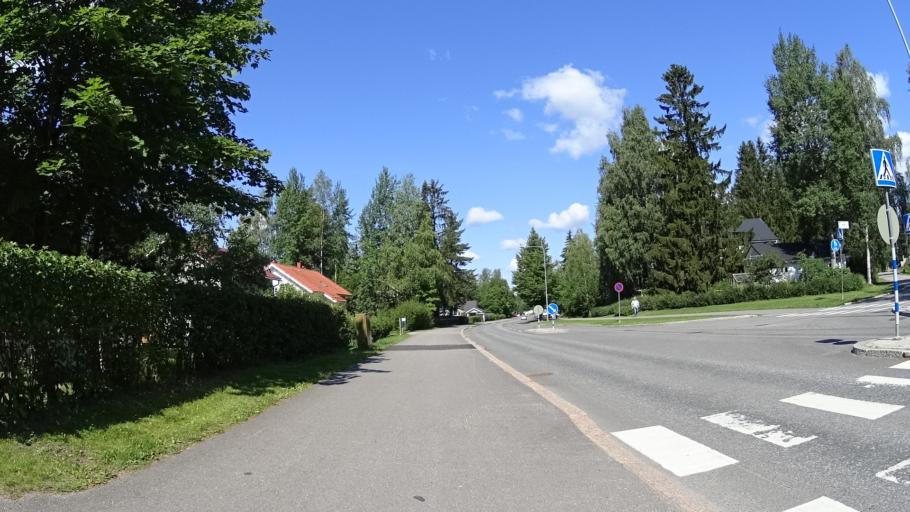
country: FI
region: Uusimaa
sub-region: Helsinki
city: Jaervenpaeae
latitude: 60.4850
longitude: 25.0727
